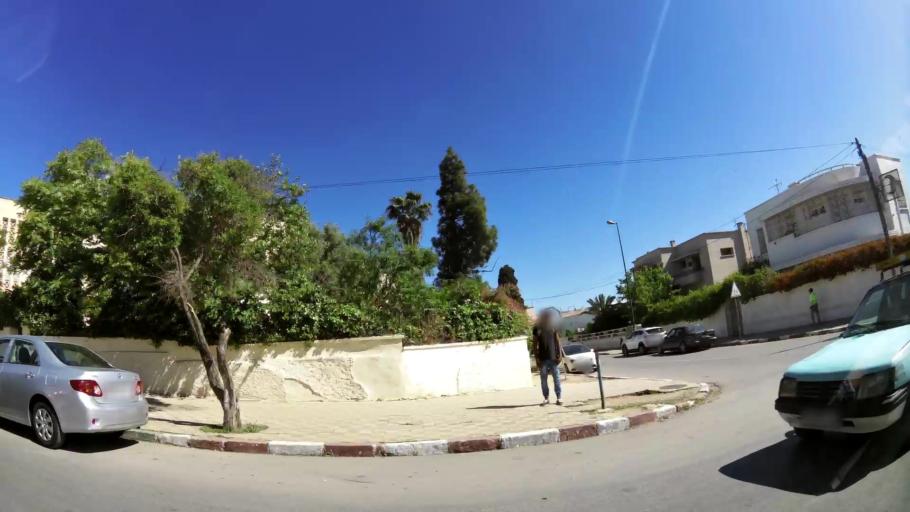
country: MA
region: Meknes-Tafilalet
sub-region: Meknes
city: Meknes
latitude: 33.9016
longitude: -5.5498
